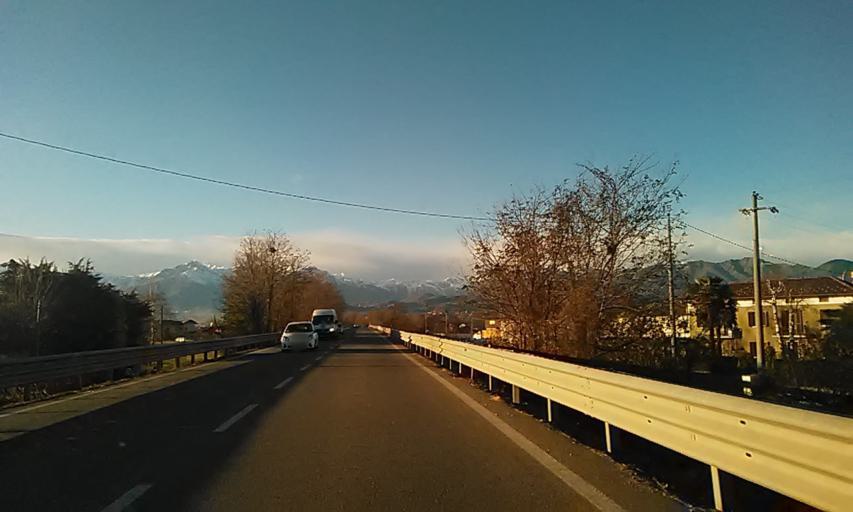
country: IT
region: Piedmont
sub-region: Provincia di Biella
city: Cerreto Castello
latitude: 45.5454
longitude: 8.1768
